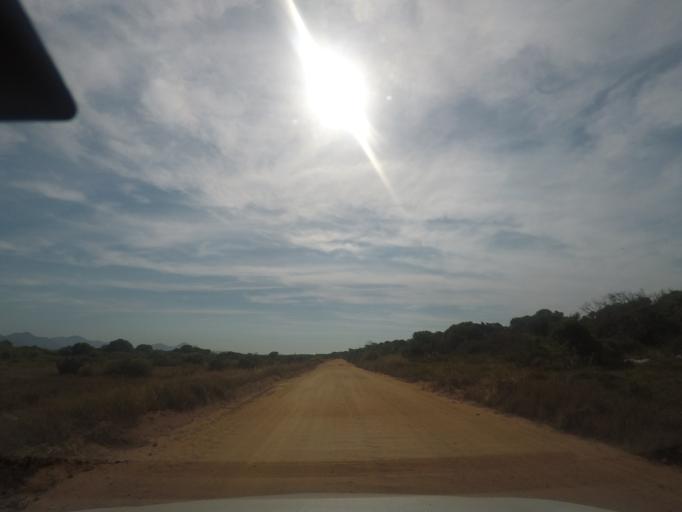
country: BR
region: Rio de Janeiro
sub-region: Marica
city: Marica
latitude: -22.9601
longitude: -42.8633
